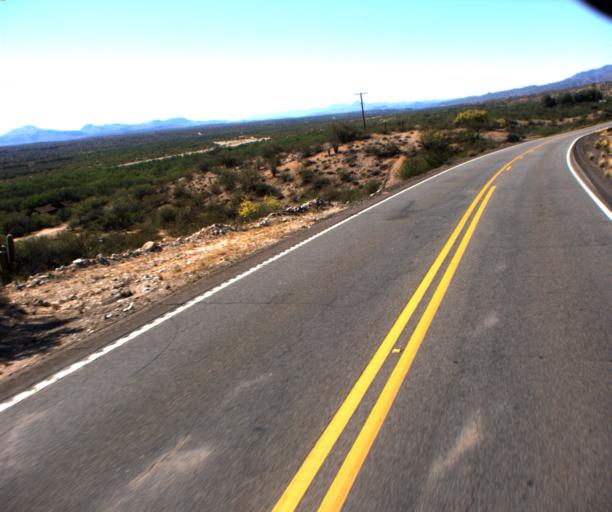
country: US
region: Arizona
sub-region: Yavapai County
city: Bagdad
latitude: 34.7943
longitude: -113.6231
